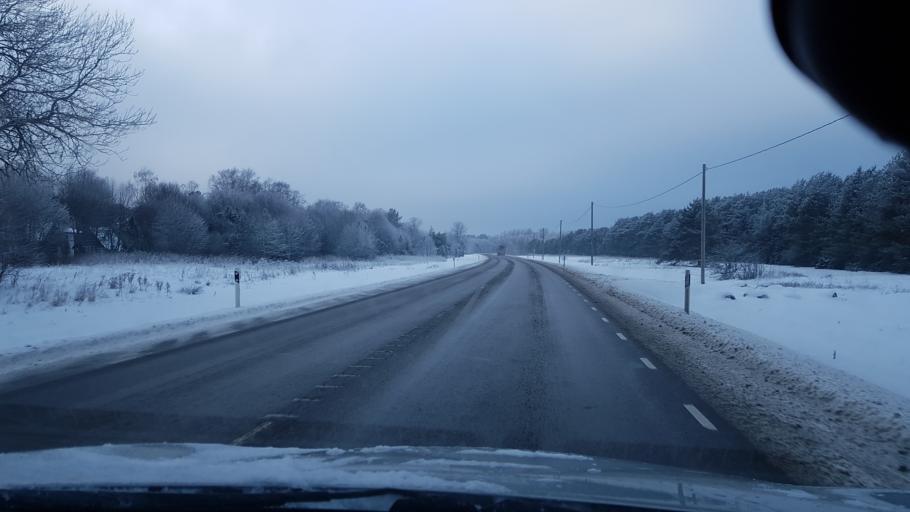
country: EE
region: Harju
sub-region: Paldiski linn
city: Paldiski
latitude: 59.3392
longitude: 24.2148
